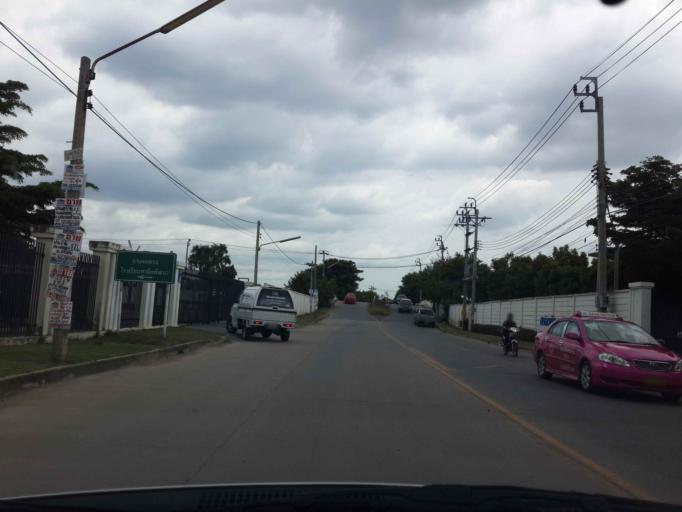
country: TH
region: Bangkok
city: Khlong Sam Wa
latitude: 13.8778
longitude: 100.7111
